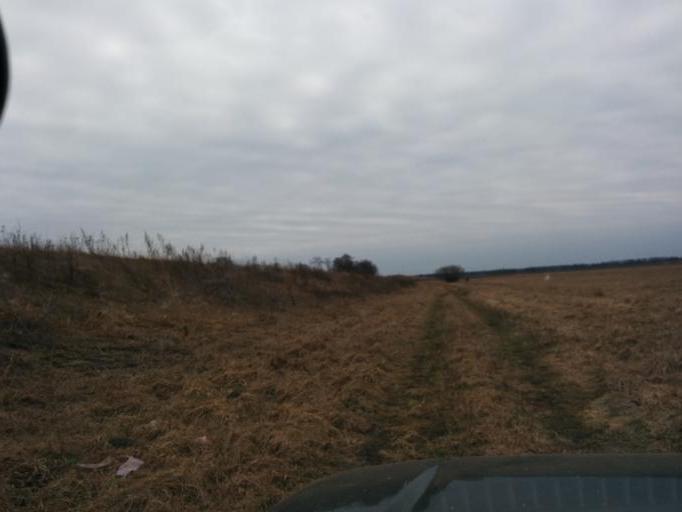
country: LV
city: Tireli
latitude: 56.9073
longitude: 23.6265
